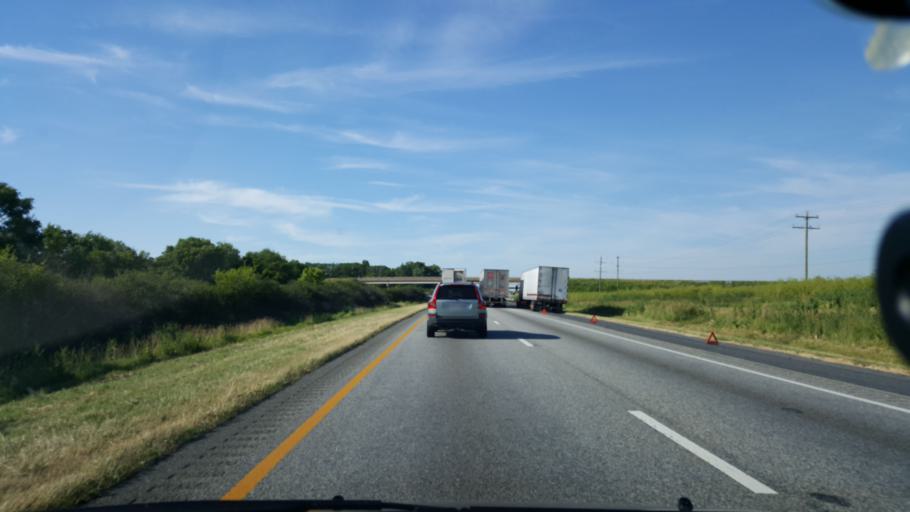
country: US
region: Virginia
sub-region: Rockingham County
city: Bridgewater
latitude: 38.3478
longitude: -78.9326
